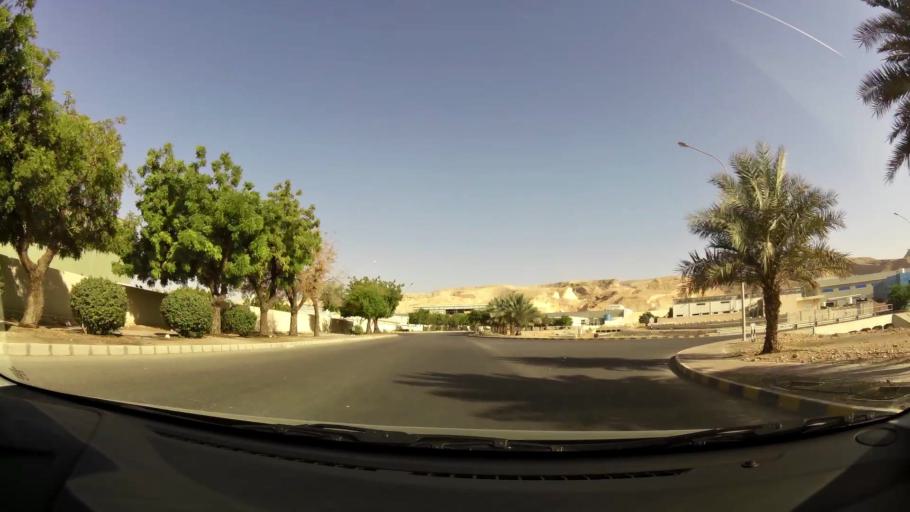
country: OM
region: Muhafazat Masqat
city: As Sib al Jadidah
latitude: 23.5540
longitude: 58.2225
